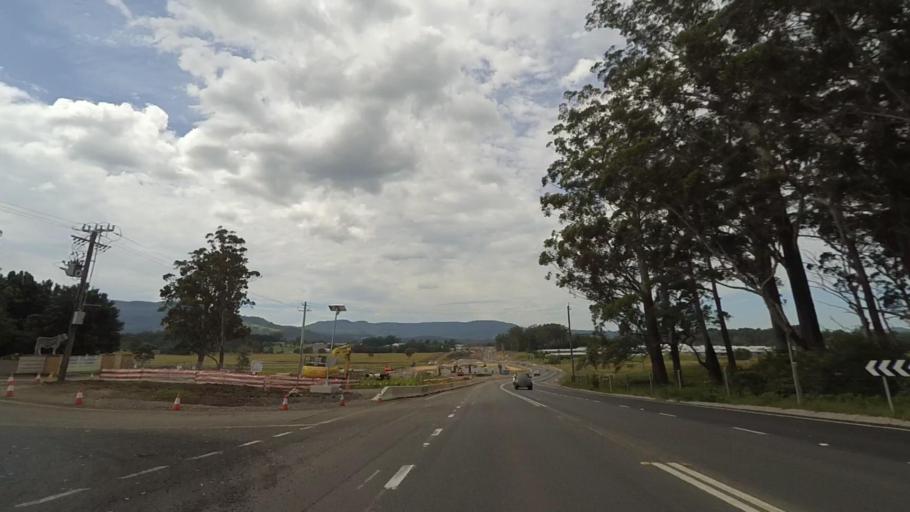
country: AU
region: New South Wales
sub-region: Shoalhaven Shire
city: Berry
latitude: -34.7825
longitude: 150.6786
